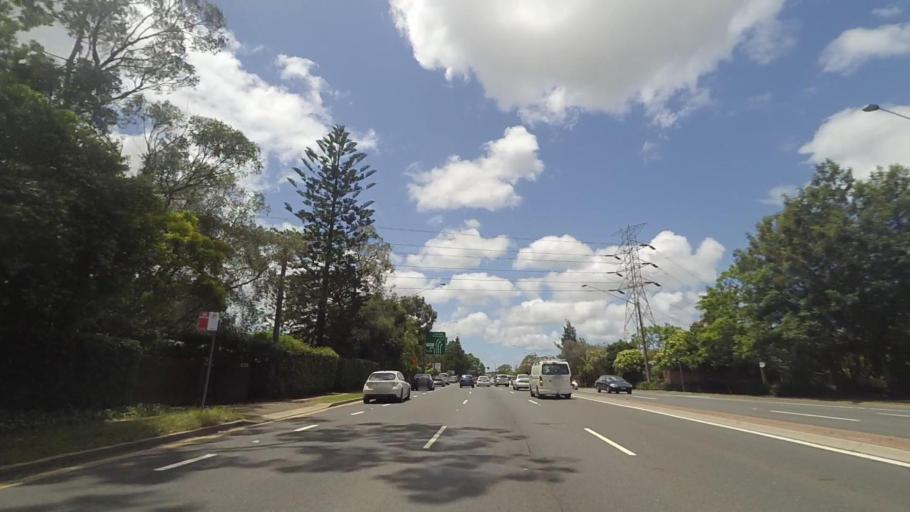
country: AU
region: New South Wales
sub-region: Hornsby Shire
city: Pennant Hills
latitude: -33.7400
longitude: 151.0642
